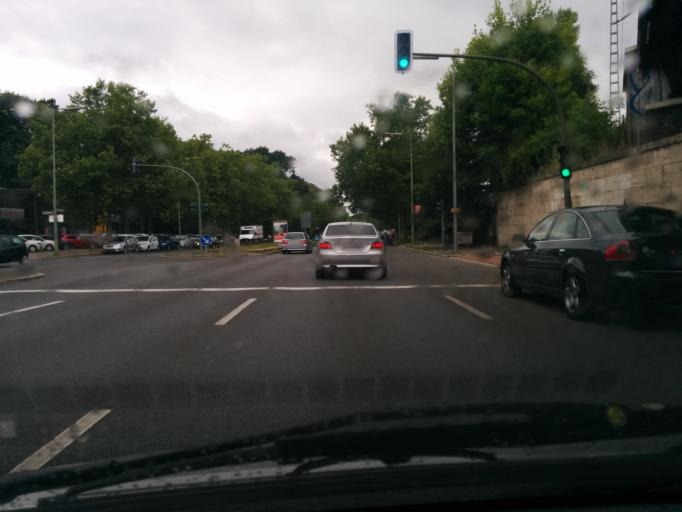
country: DE
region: Berlin
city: Haselhorst
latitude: 52.5250
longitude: 13.2456
